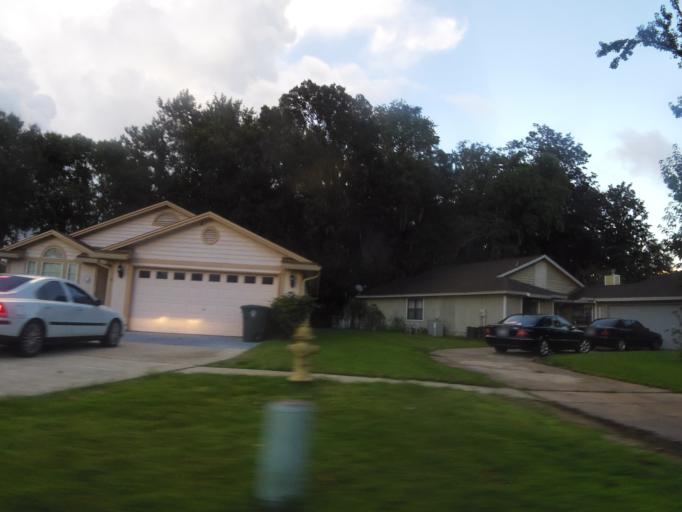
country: US
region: Florida
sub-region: Duval County
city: Jacksonville
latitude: 30.2303
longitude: -81.6055
